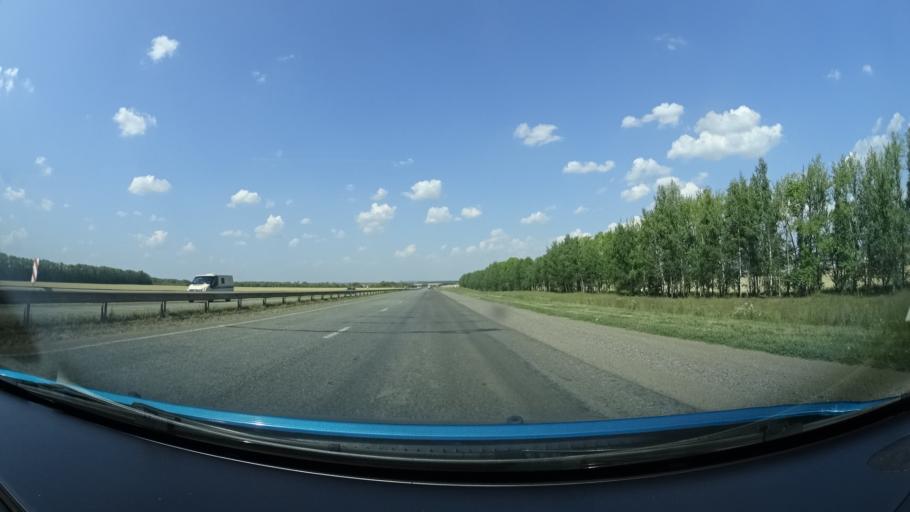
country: RU
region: Bashkortostan
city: Dmitriyevka
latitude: 54.6742
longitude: 55.3644
